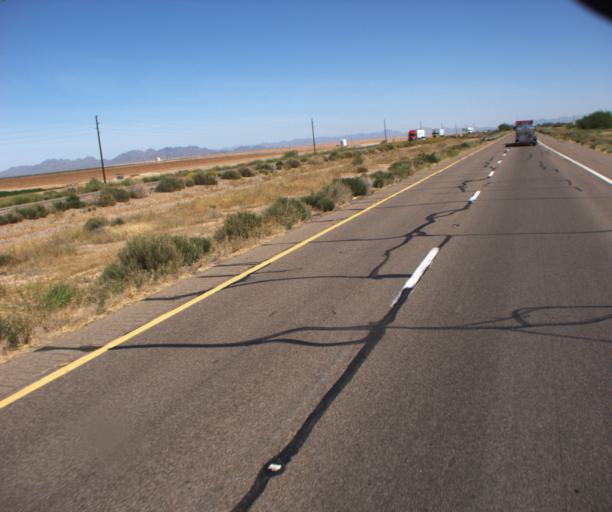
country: US
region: Arizona
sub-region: Maricopa County
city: Gila Bend
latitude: 32.9225
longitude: -112.8815
